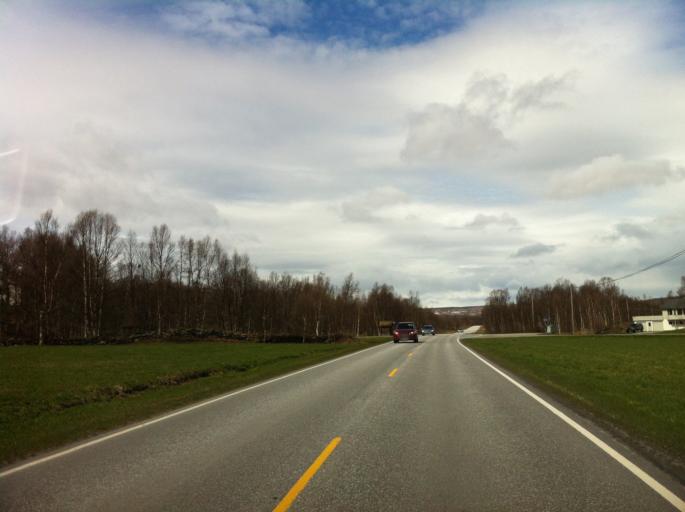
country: NO
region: Sor-Trondelag
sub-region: Roros
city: Roros
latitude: 62.6001
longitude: 11.6766
